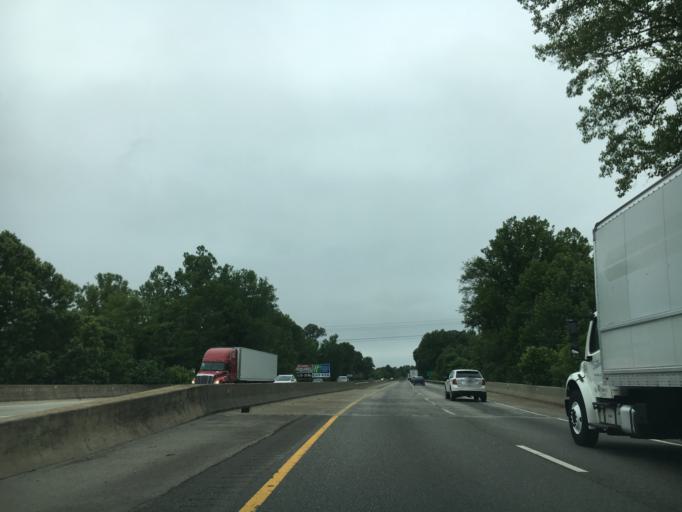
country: US
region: Virginia
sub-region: Chesterfield County
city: Ettrick
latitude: 37.2000
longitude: -77.4429
